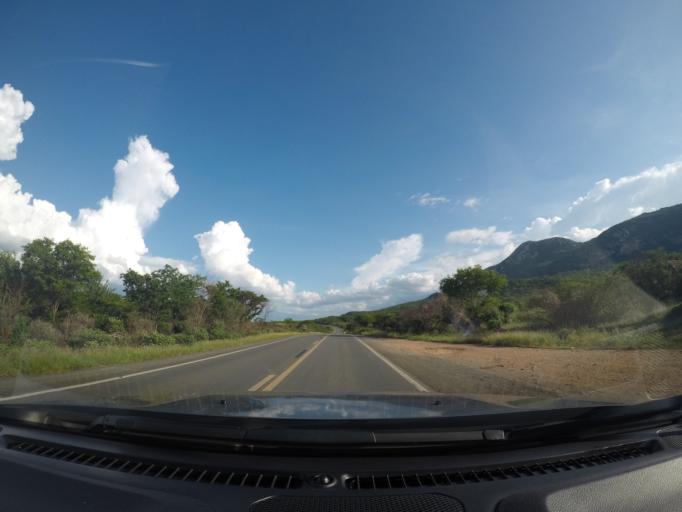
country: BR
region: Bahia
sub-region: Oliveira Dos Brejinhos
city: Oliveira dos Brejinhos
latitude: -12.0621
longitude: -42.9611
